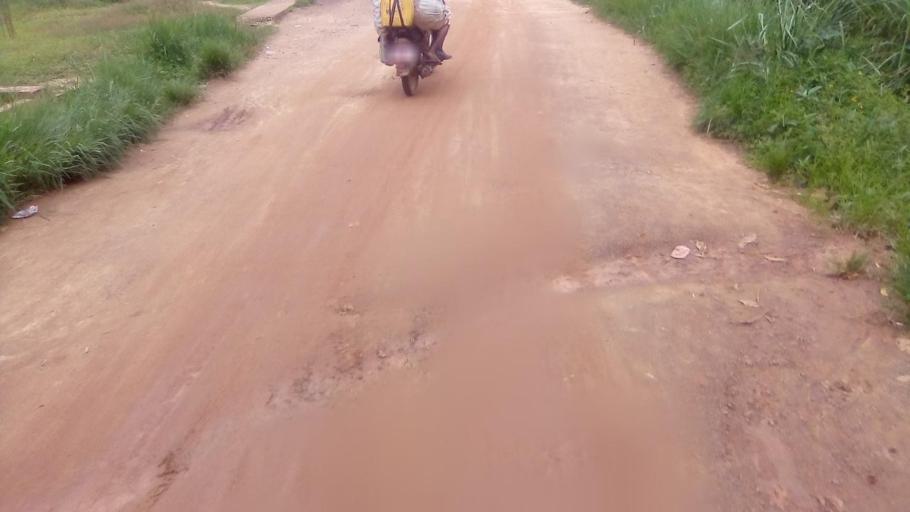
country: SL
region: Southern Province
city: Bo
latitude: 7.9412
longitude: -11.7422
